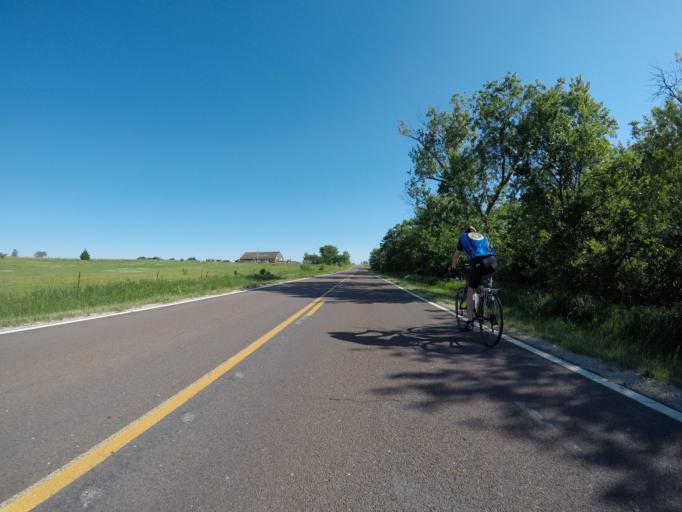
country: US
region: Kansas
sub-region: Lyon County
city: Emporia
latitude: 38.6628
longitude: -96.0975
